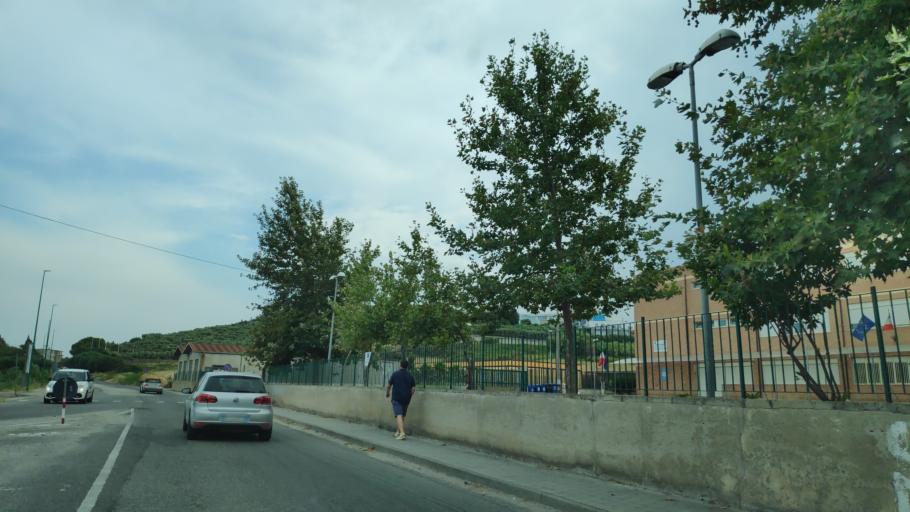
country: IT
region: Calabria
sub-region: Provincia di Catanzaro
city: Soverato Marina
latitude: 38.6846
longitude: 16.5481
